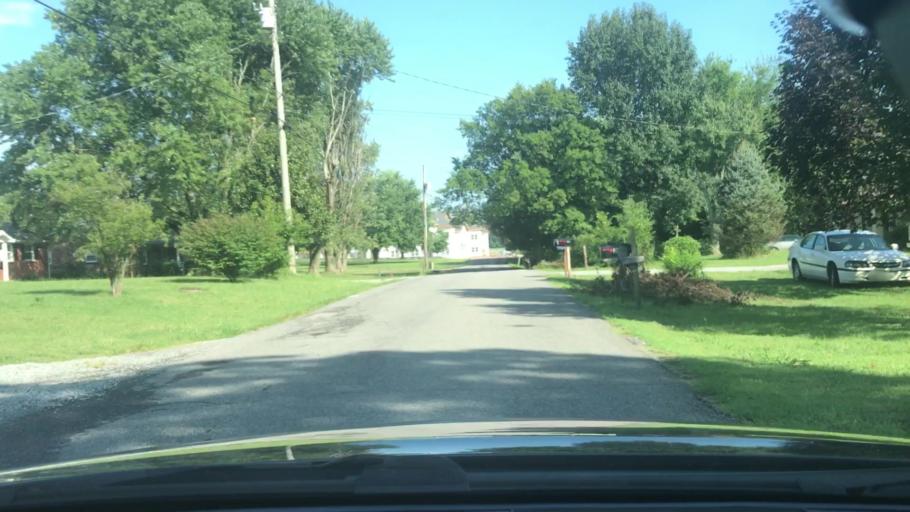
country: US
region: Tennessee
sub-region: Sumner County
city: White House
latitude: 36.4555
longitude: -86.6733
